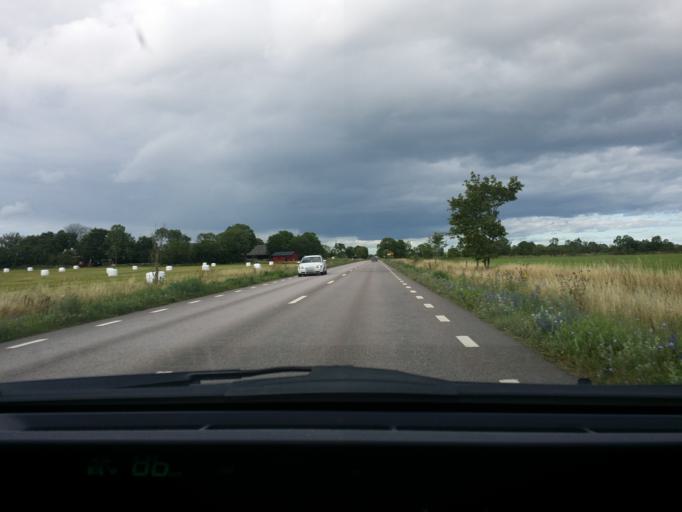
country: SE
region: Kalmar
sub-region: Borgholms Kommun
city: Borgholm
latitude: 56.9154
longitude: 16.7463
